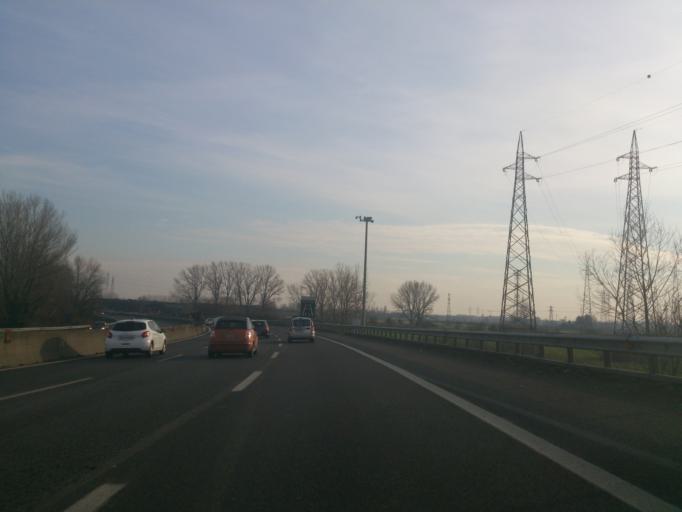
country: IT
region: Lombardy
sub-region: Citta metropolitana di Milano
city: Chiaravalle
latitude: 45.4193
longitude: 9.2462
